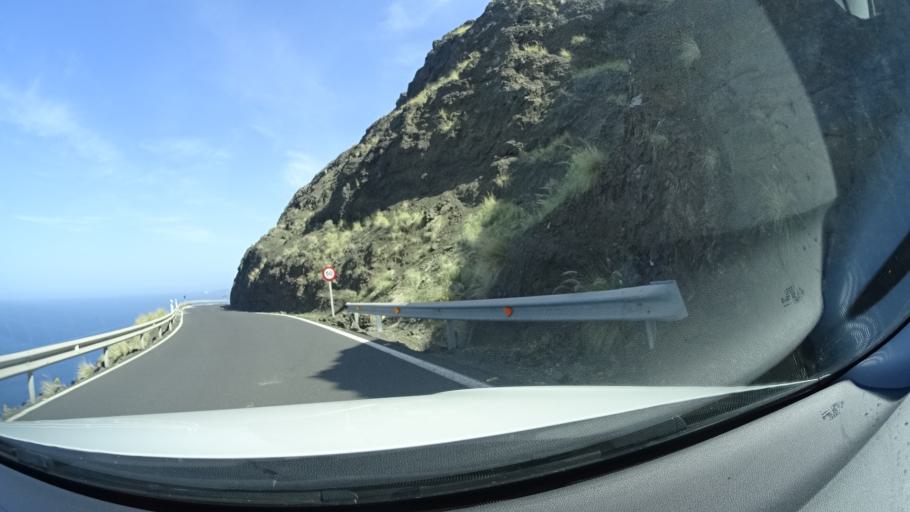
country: ES
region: Canary Islands
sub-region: Provincia de Las Palmas
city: Agaete
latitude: 28.0652
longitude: -15.7247
